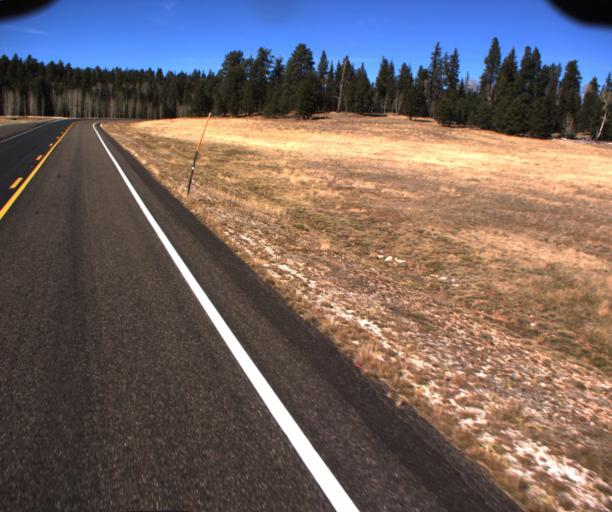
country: US
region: Arizona
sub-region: Coconino County
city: Grand Canyon
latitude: 36.5028
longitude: -112.1391
